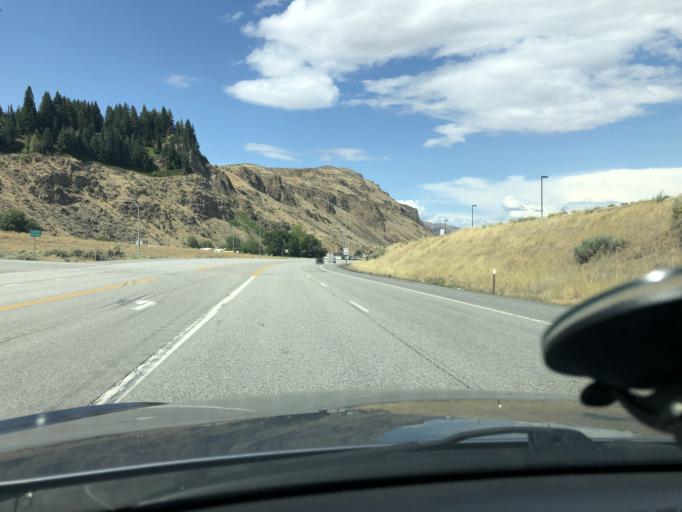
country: US
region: Washington
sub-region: Chelan County
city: Sunnyslope
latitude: 47.4736
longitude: -120.3247
